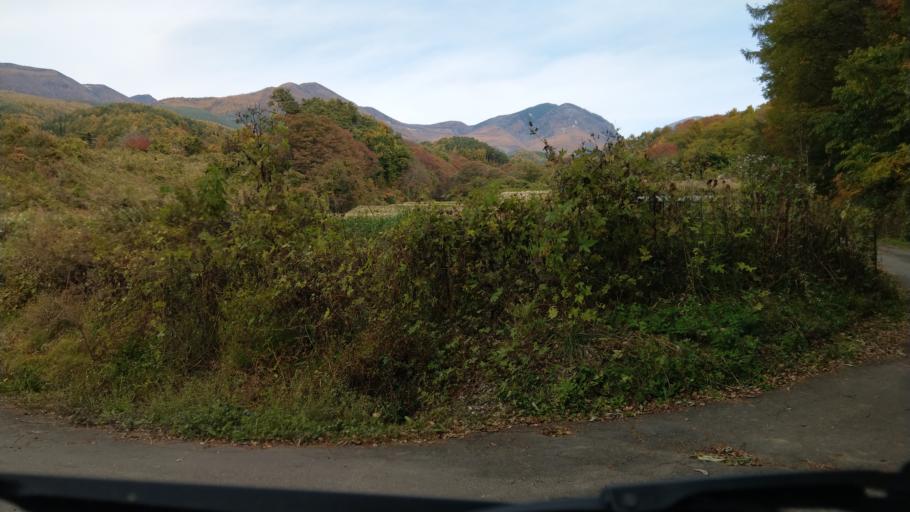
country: JP
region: Nagano
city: Komoro
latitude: 36.3510
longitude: 138.4354
